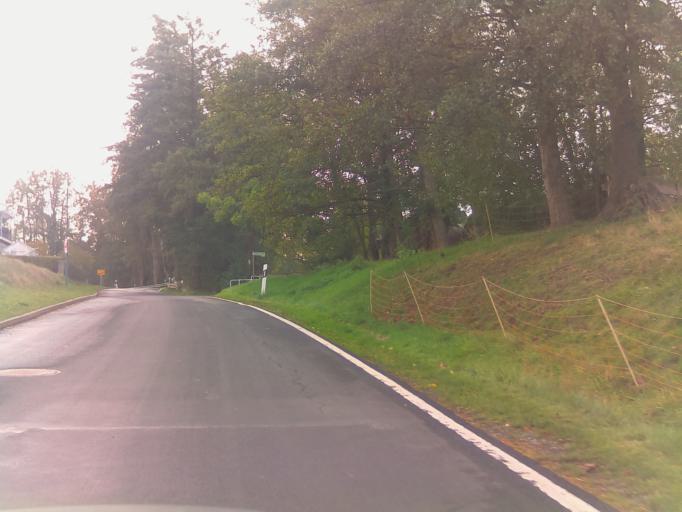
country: DE
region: Hesse
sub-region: Regierungsbezirk Kassel
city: Hofbieber
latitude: 50.5785
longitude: 9.8062
